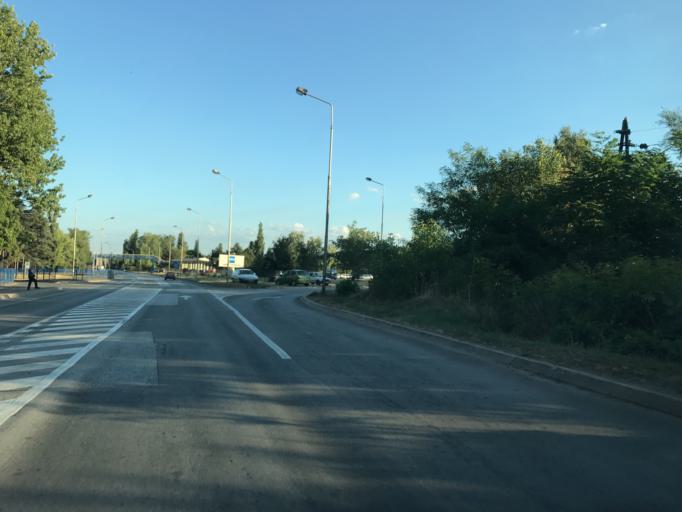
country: RS
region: Central Serbia
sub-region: Podunavski Okrug
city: Smederevo
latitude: 44.6068
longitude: 20.9611
